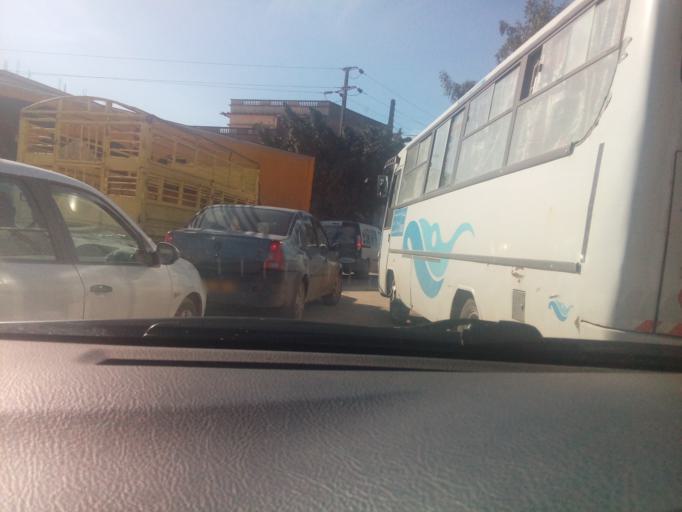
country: DZ
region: Oran
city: Sidi ech Chahmi
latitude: 35.6527
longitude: -0.5681
